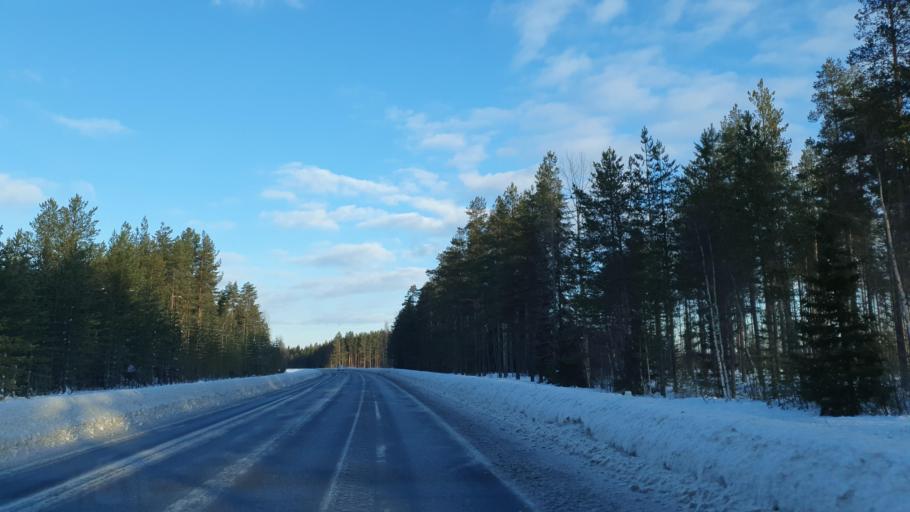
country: FI
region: Northern Ostrobothnia
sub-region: Oulunkaari
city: Utajaervi
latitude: 64.6945
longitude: 26.5374
